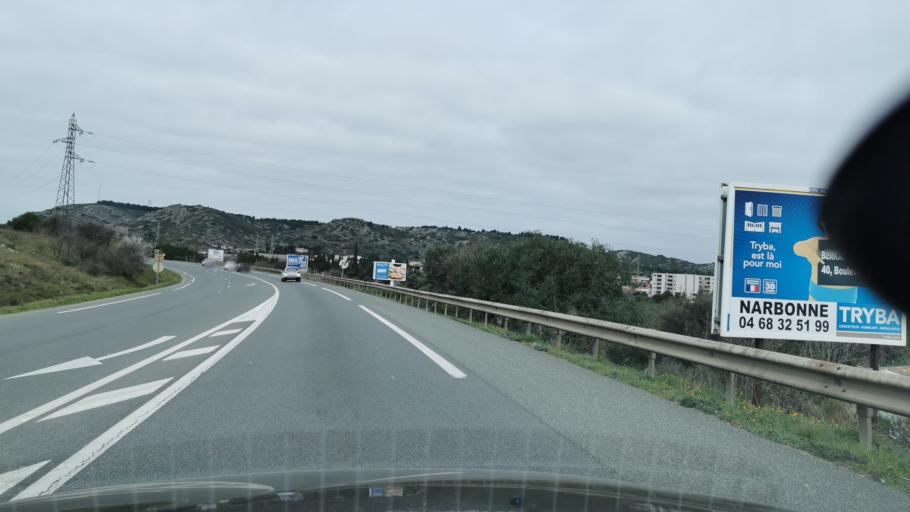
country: FR
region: Languedoc-Roussillon
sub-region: Departement de l'Aude
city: Narbonne
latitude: 43.1765
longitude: 2.9728
